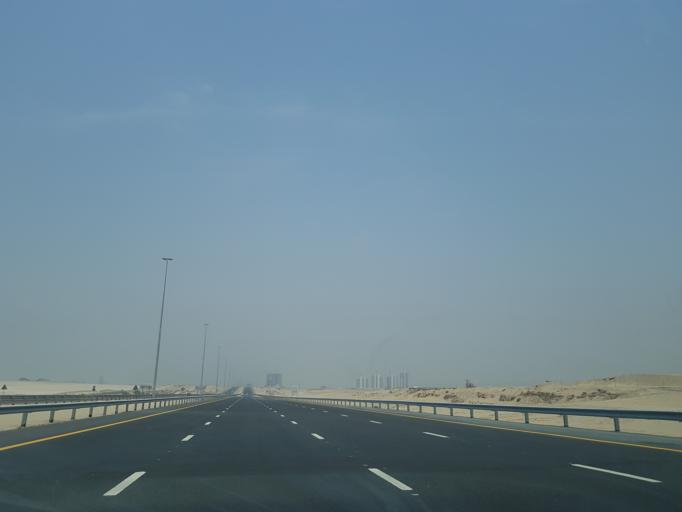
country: AE
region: Dubai
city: Dubai
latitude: 25.0116
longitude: 55.2170
